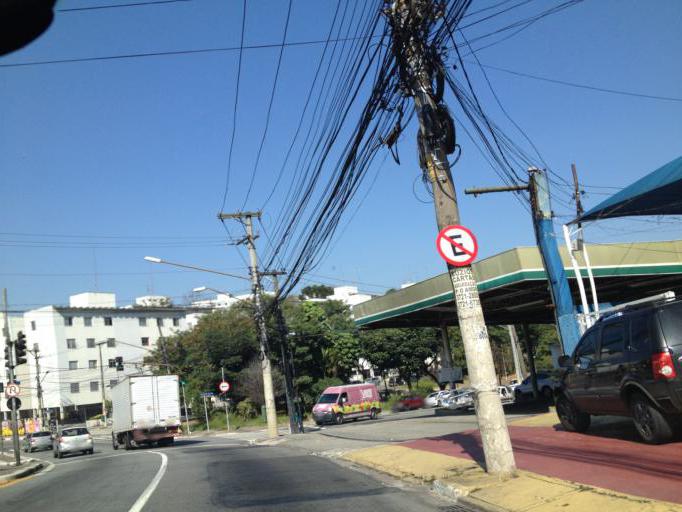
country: BR
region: Sao Paulo
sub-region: Osasco
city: Osasco
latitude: -23.5746
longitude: -46.7301
